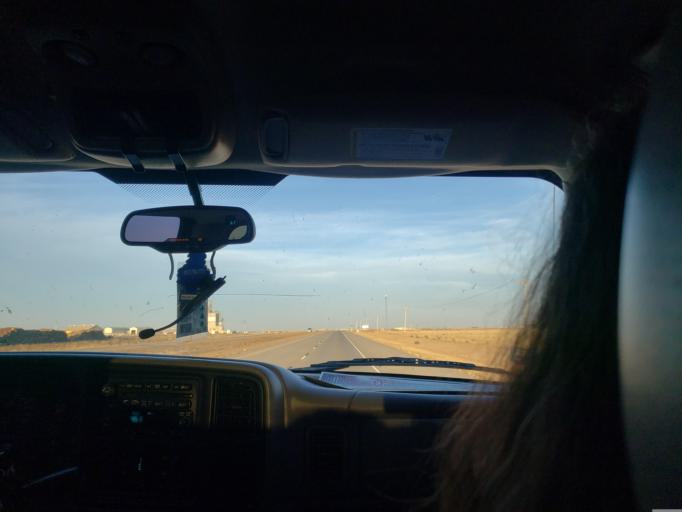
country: US
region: Oklahoma
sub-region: Texas County
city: Guymon
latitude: 36.7657
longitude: -101.3482
